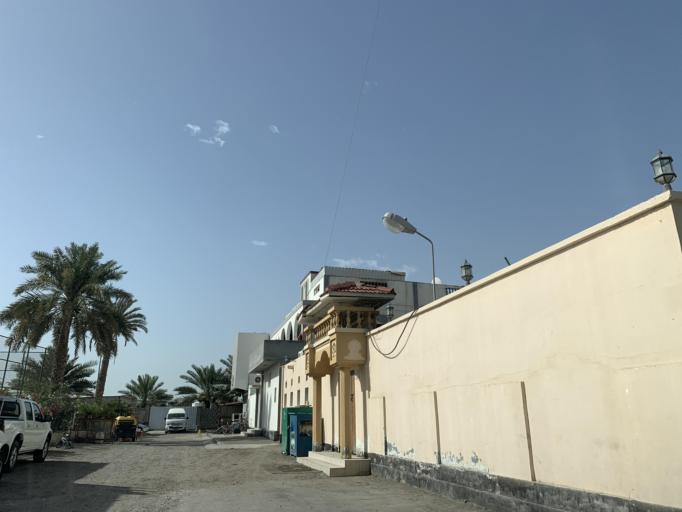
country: BH
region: Northern
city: Sitrah
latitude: 26.1456
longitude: 50.6125
